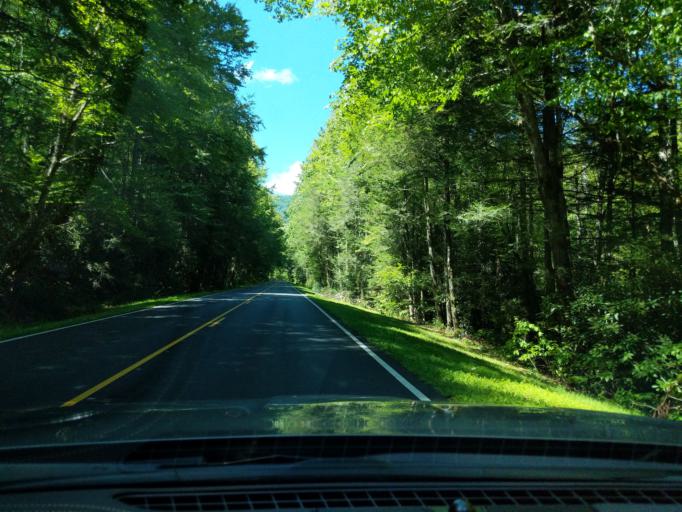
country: US
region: North Carolina
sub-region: Swain County
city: Cherokee
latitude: 35.5711
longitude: -83.3383
